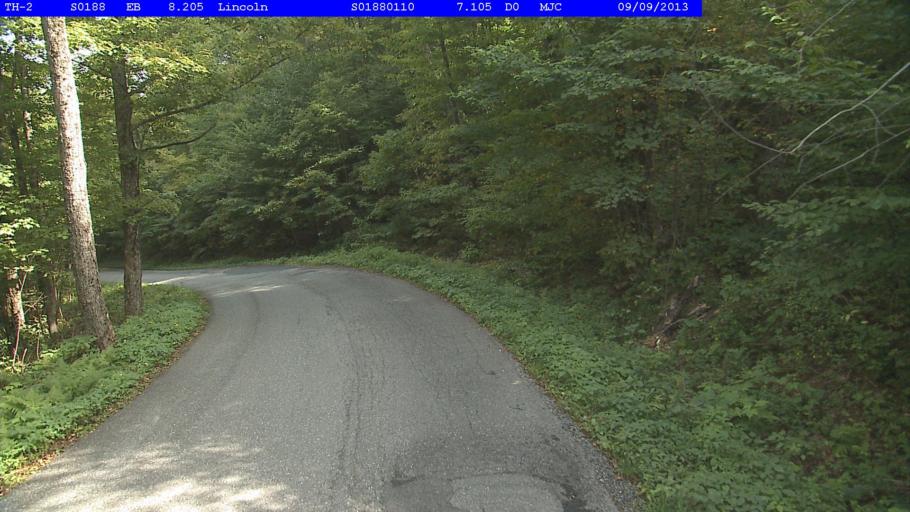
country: US
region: Vermont
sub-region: Addison County
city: Bristol
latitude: 44.0946
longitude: -72.9254
